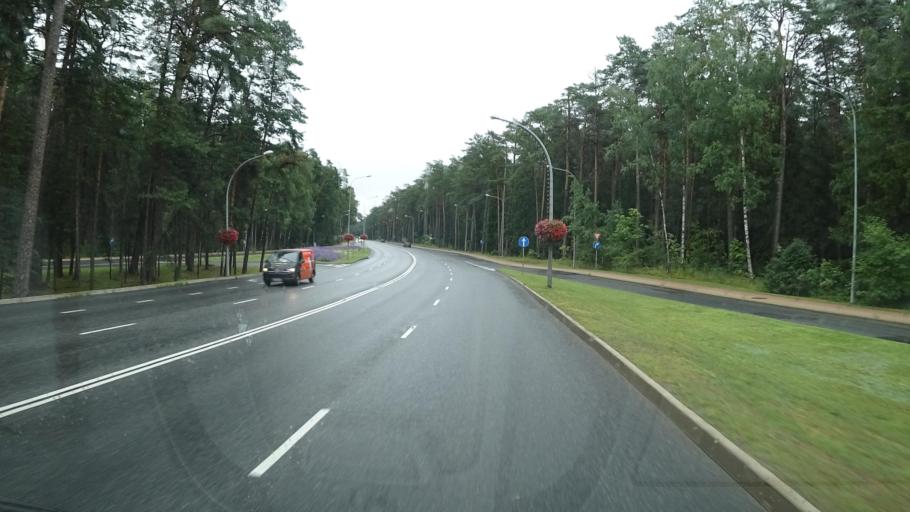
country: LV
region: Jurmala
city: Jurmala
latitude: 56.9725
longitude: 23.8315
